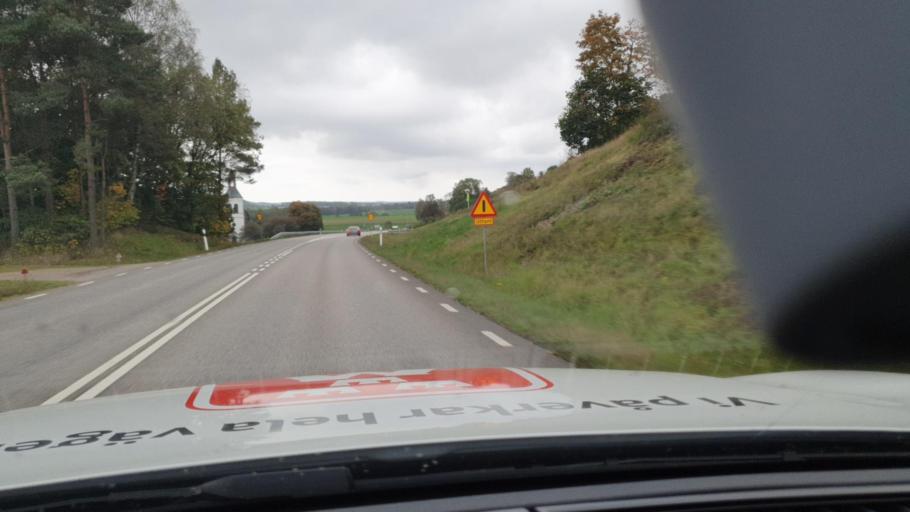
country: SE
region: Halland
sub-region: Falkenbergs Kommun
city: Falkenberg
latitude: 56.9940
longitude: 12.5854
